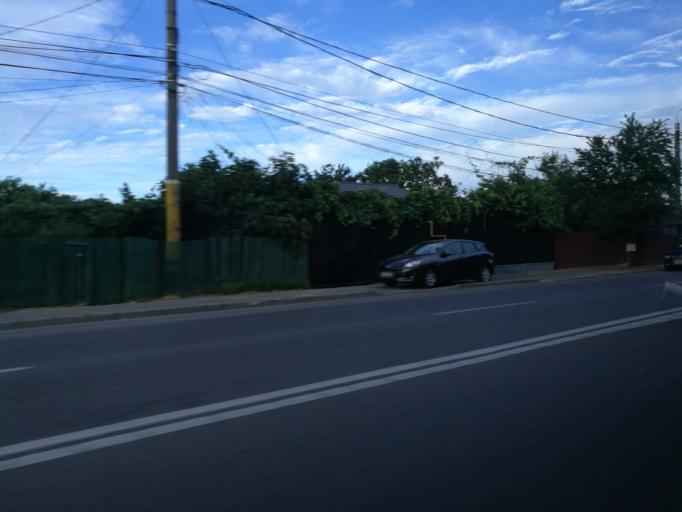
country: RO
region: Constanta
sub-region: Municipiul Constanta
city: Constanta
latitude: 44.1523
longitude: 28.6217
